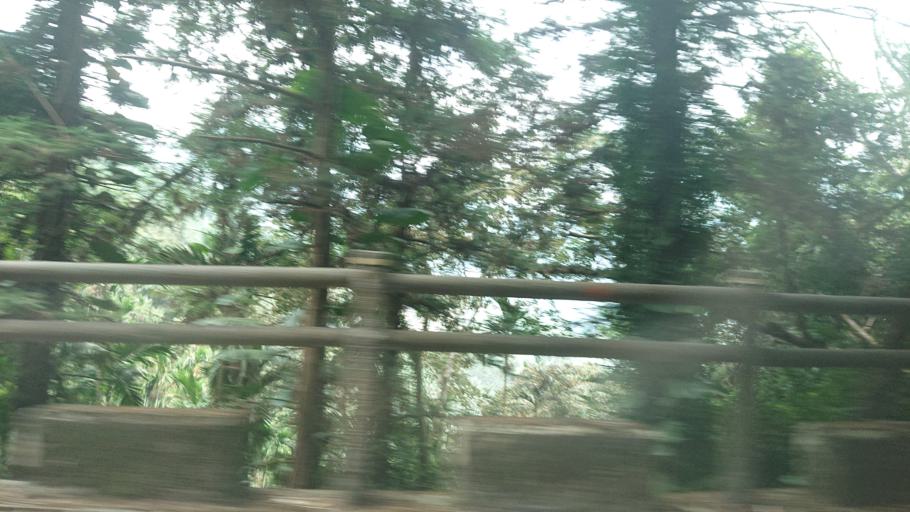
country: TW
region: Taiwan
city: Lugu
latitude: 23.5858
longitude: 120.6981
